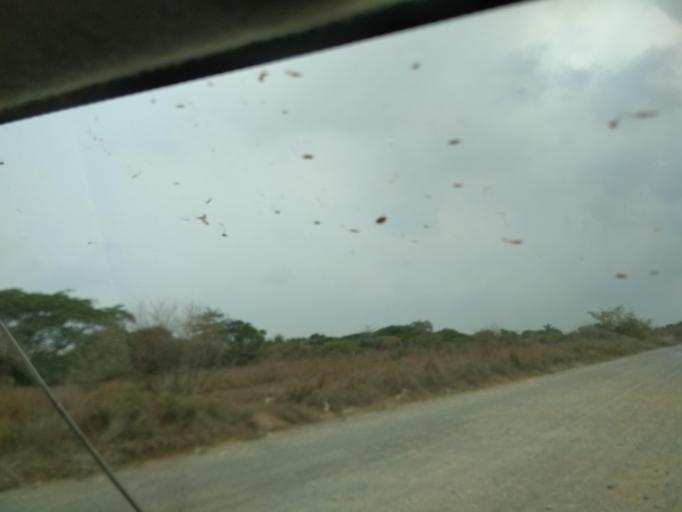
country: MX
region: Veracruz
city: Paso del Toro
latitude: 19.0075
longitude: -96.1116
